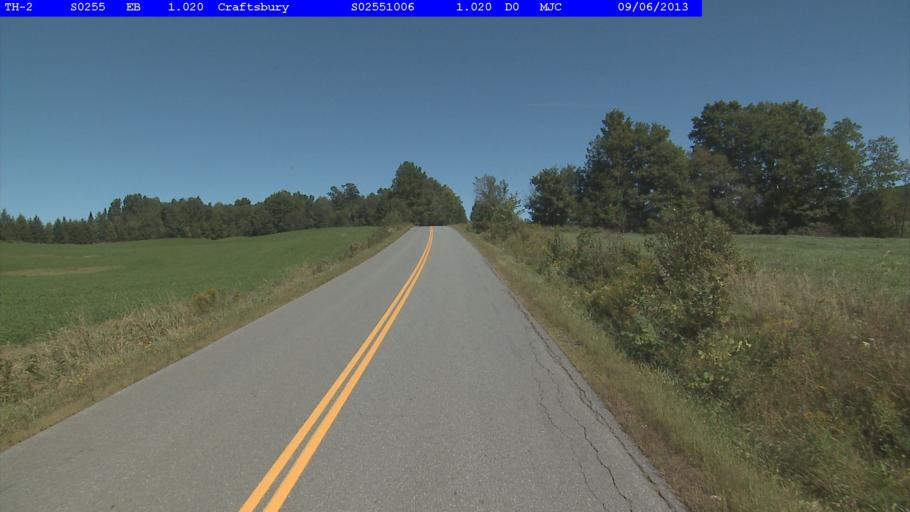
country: US
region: Vermont
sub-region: Caledonia County
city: Hardwick
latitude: 44.6324
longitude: -72.3490
